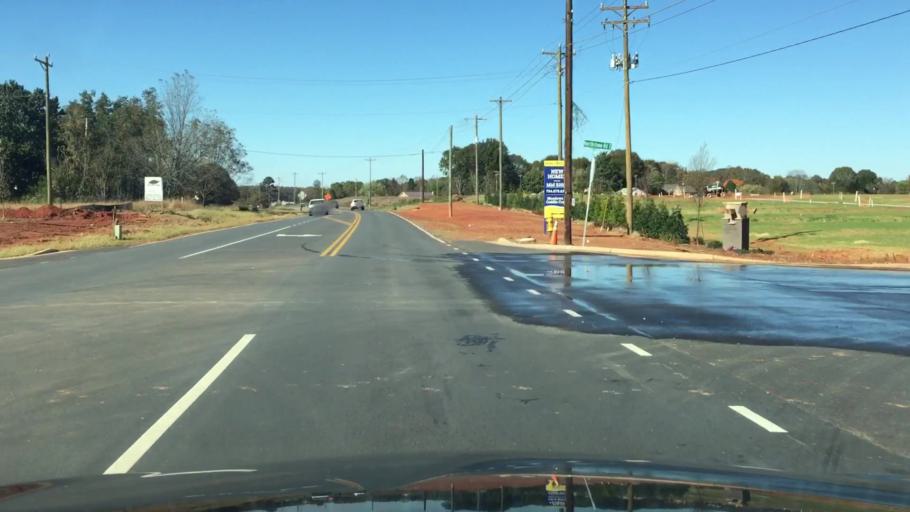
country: US
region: North Carolina
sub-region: Iredell County
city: Mooresville
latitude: 35.5493
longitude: -80.7732
